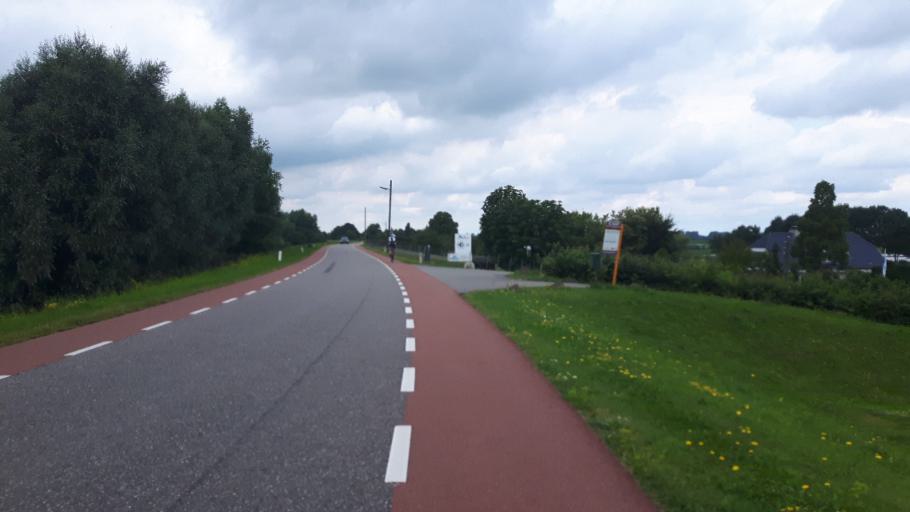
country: NL
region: South Holland
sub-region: Molenwaard
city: Liesveld
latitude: 51.9185
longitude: 4.7761
